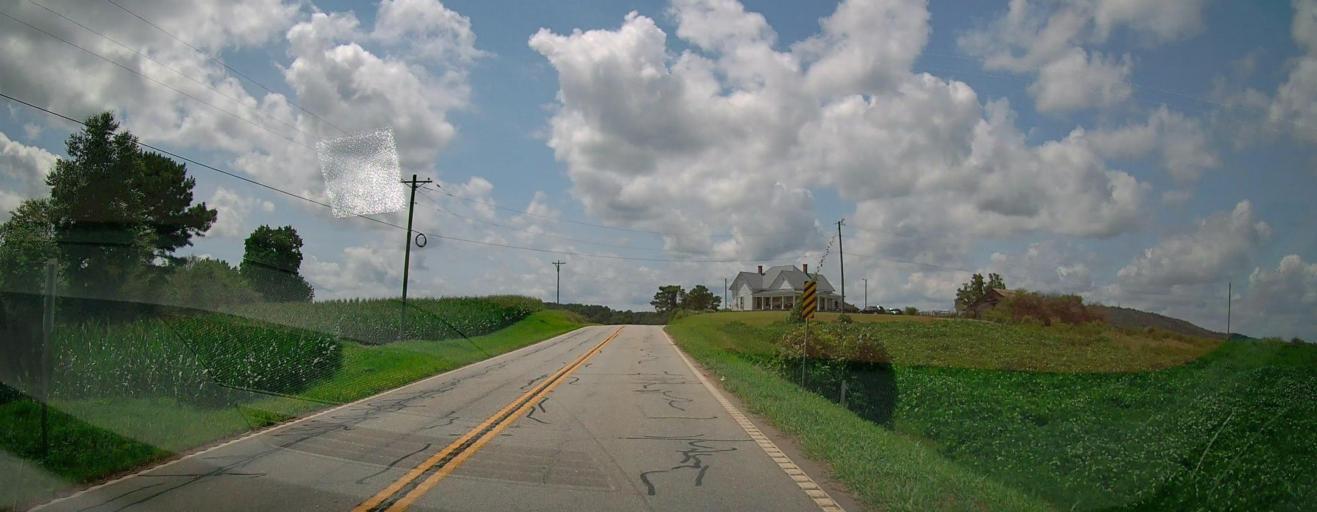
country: US
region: Georgia
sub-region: Carroll County
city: Bowdon
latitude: 33.4143
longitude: -85.2584
